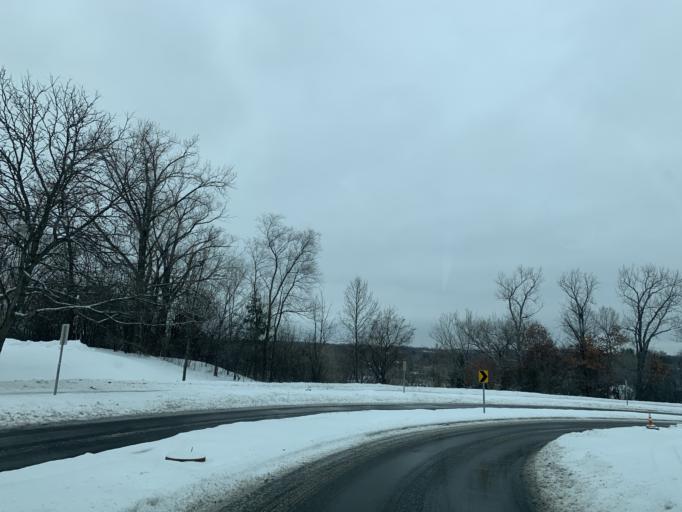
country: US
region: Minnesota
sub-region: Ramsey County
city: Roseville
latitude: 44.9903
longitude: -93.1145
